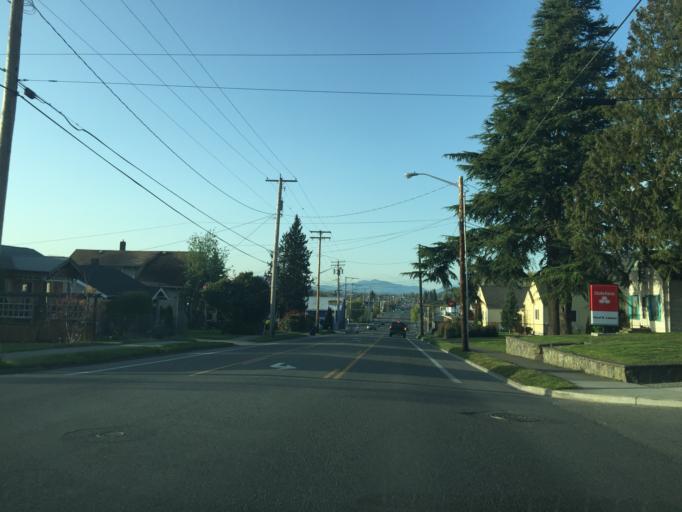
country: US
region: Washington
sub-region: Skagit County
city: Mount Vernon
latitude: 48.4263
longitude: -122.3354
